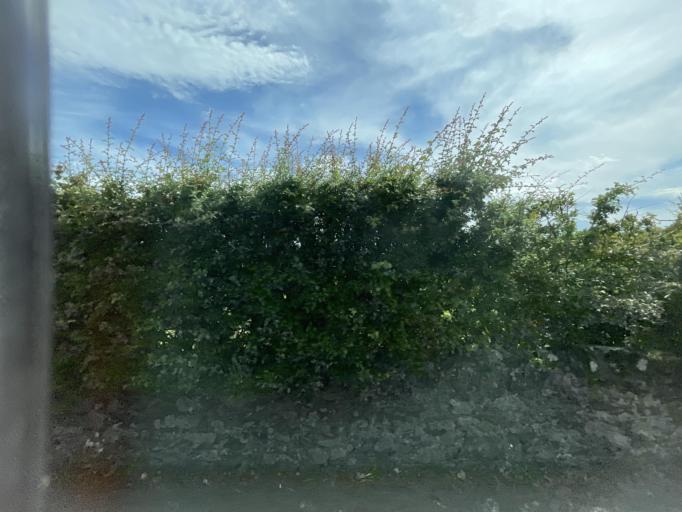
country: GB
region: Wales
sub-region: Anglesey
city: Llanfachraeth
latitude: 53.2683
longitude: -4.4690
